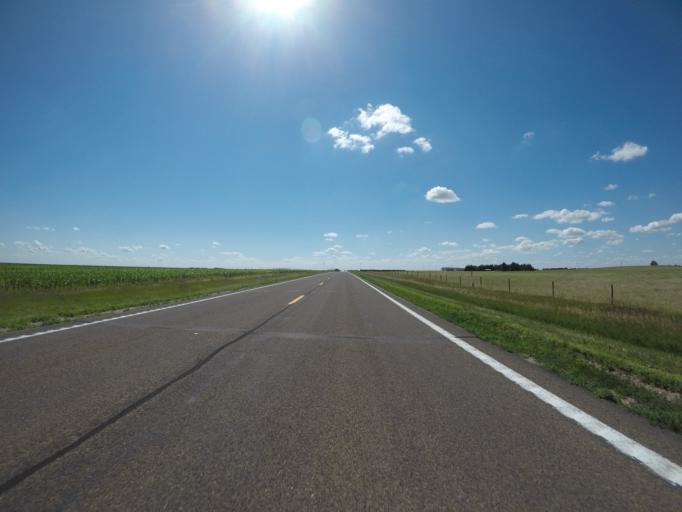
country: US
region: Nebraska
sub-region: Chase County
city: Imperial
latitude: 40.5377
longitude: -101.8715
